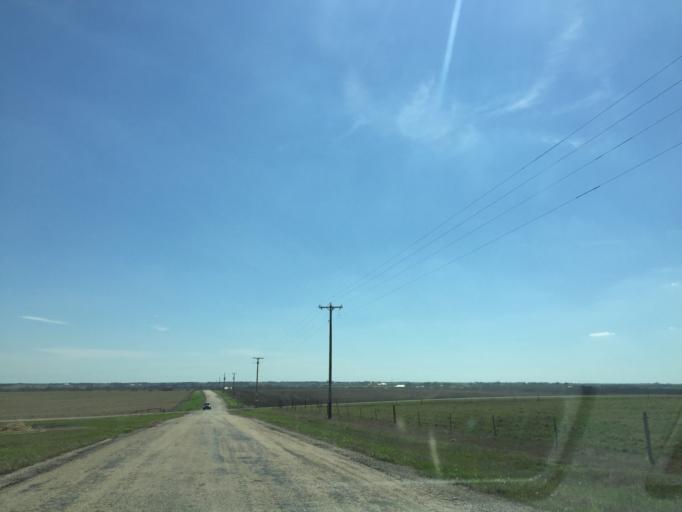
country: US
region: Texas
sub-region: Williamson County
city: Taylor
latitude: 30.5547
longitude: -97.3231
